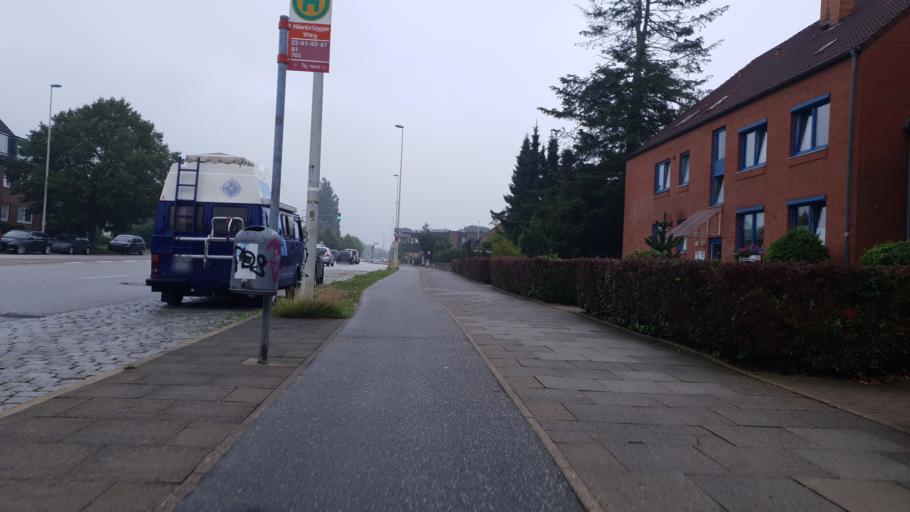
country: DE
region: Schleswig-Holstein
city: Kronshagen
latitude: 54.3562
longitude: 10.0850
